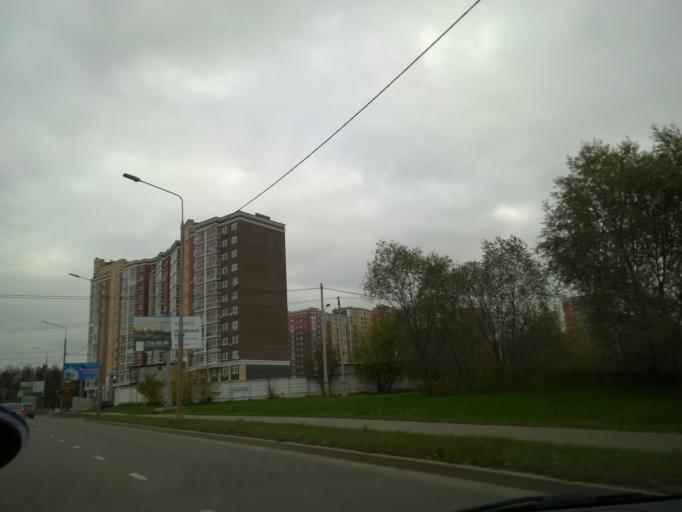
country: RU
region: Moskovskaya
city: Kommunarka
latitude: 55.5645
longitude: 37.4863
